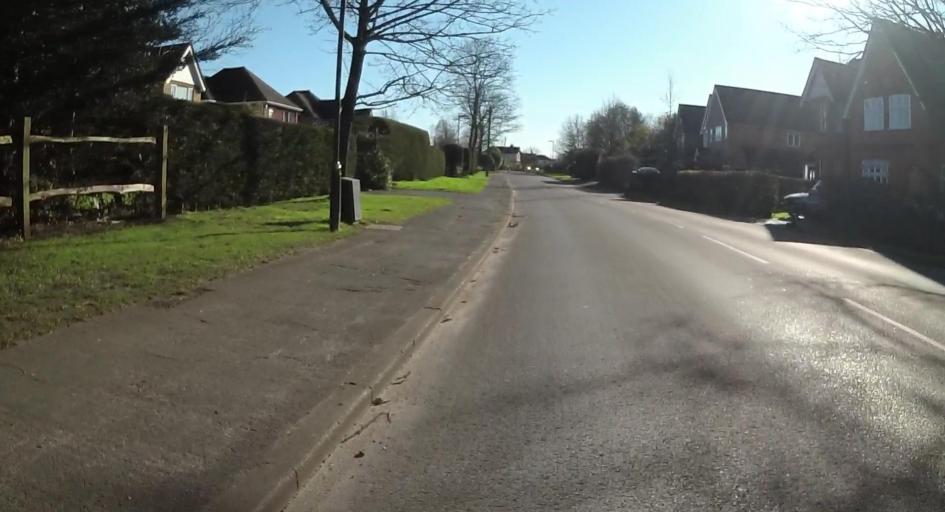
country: GB
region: England
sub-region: Surrey
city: Knaphill
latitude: 51.3198
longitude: -0.6230
